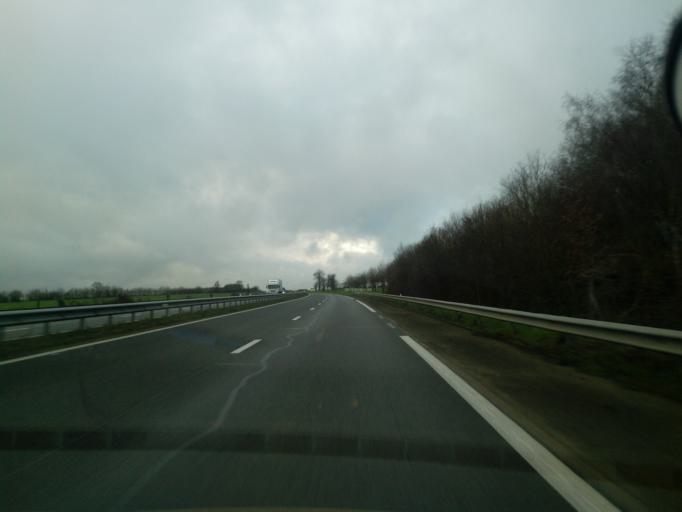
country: FR
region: Brittany
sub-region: Departement d'Ille-et-Vilaine
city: Saint-Meen-le-Grand
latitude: 48.2007
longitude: -2.2390
